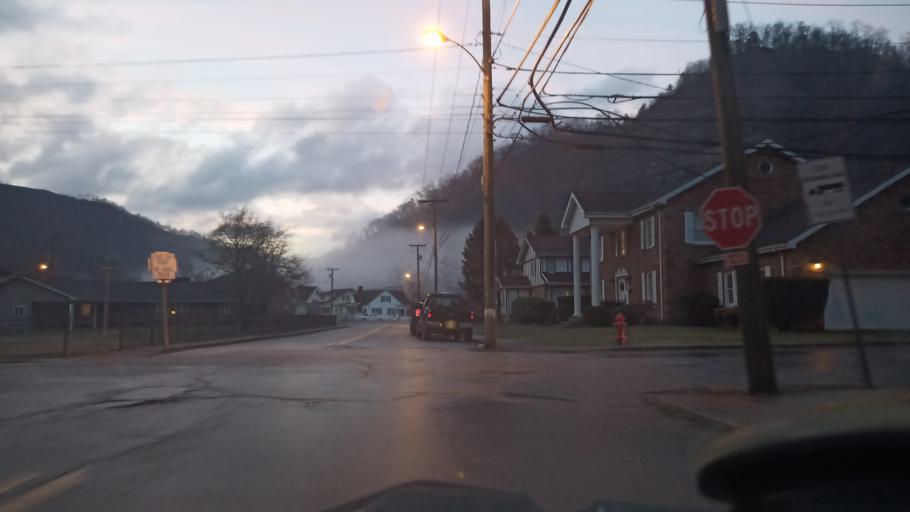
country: US
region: West Virginia
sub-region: Logan County
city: Mallory
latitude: 37.7397
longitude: -81.8777
